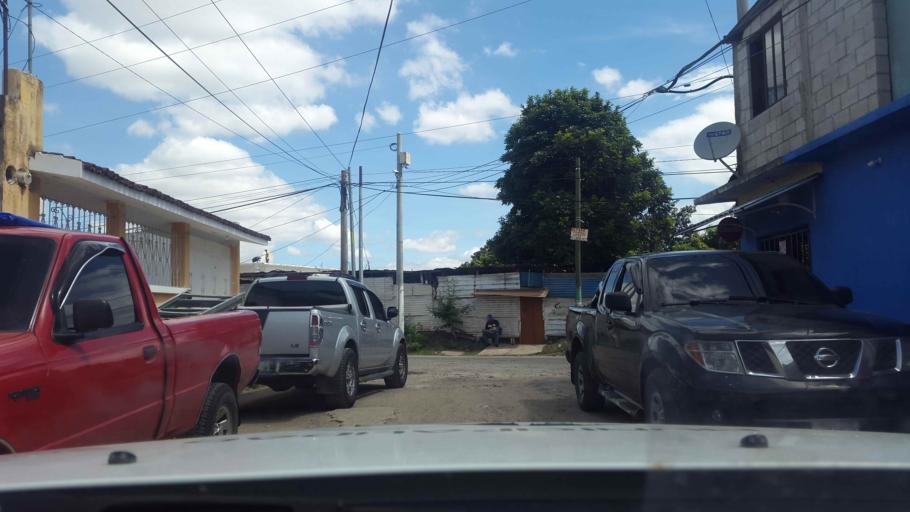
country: GT
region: Guatemala
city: Petapa
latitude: 14.5005
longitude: -90.5673
